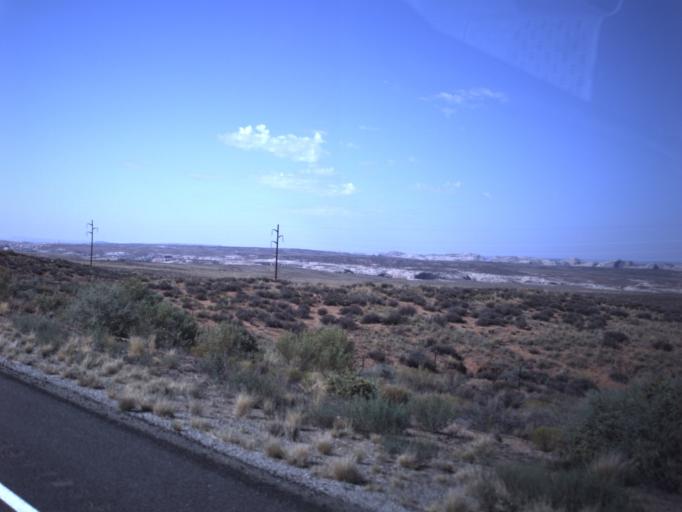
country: US
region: Utah
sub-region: San Juan County
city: Blanding
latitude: 37.3550
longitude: -109.5177
